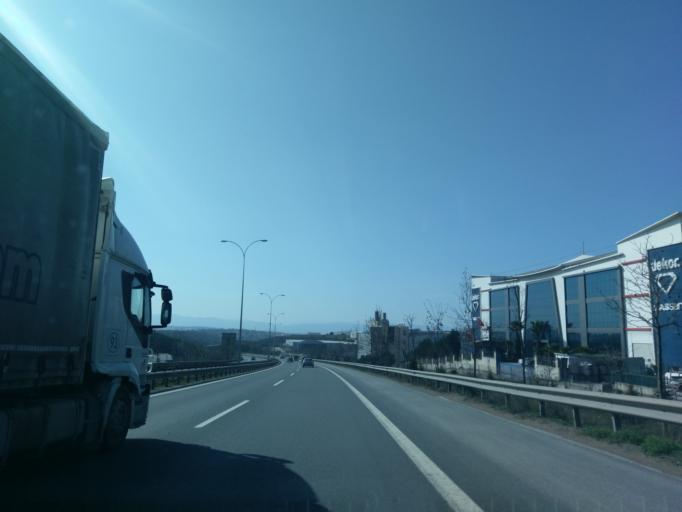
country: TR
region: Kocaeli
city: Balcik
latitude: 40.8547
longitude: 29.3754
